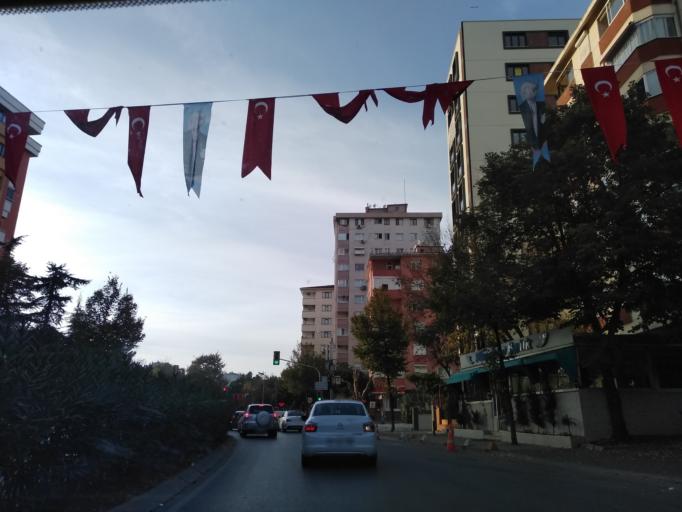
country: TR
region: Istanbul
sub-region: Atasehir
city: Atasehir
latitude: 40.9750
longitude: 29.0924
